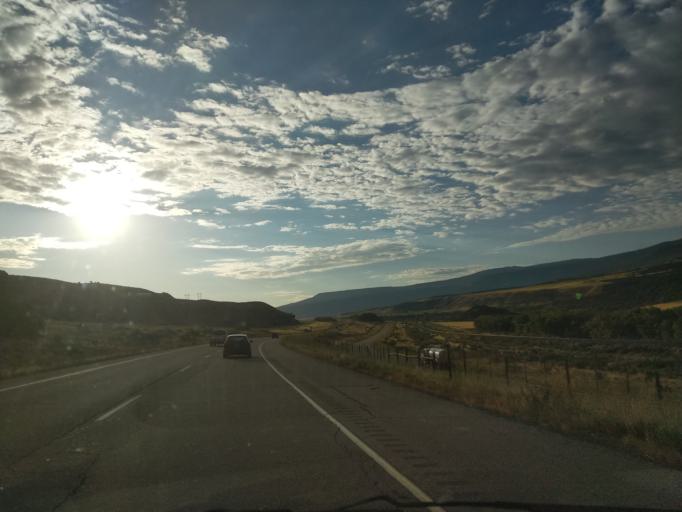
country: US
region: Colorado
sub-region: Garfield County
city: Battlement Mesa
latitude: 39.5009
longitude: -107.9321
